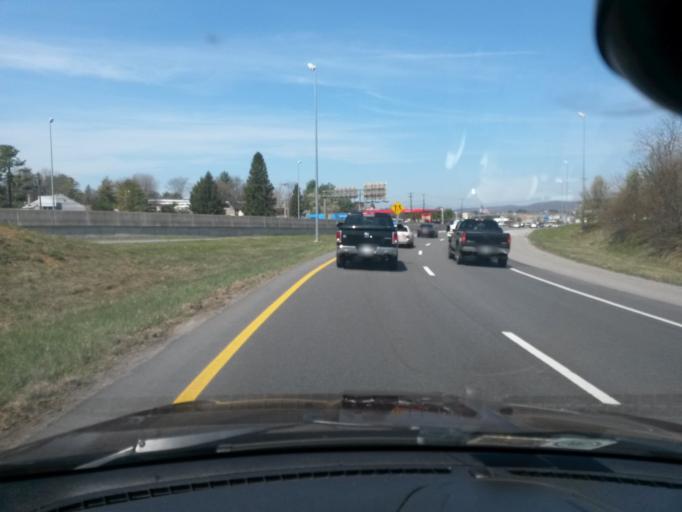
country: US
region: Virginia
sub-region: Montgomery County
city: Christiansburg
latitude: 37.1565
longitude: -80.4155
